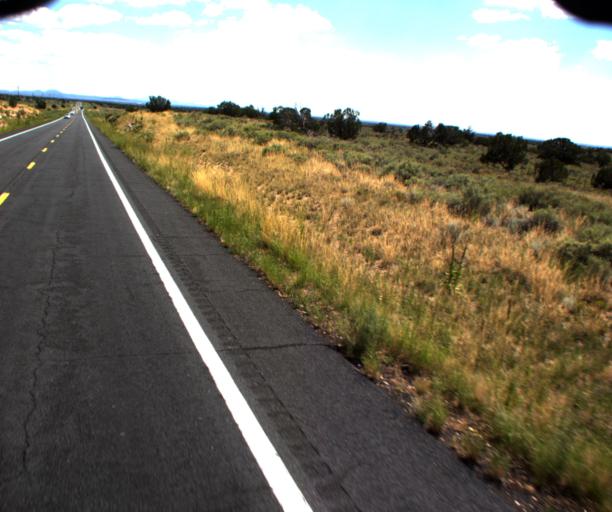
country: US
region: Arizona
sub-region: Coconino County
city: Grand Canyon Village
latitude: 35.7372
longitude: -112.1311
